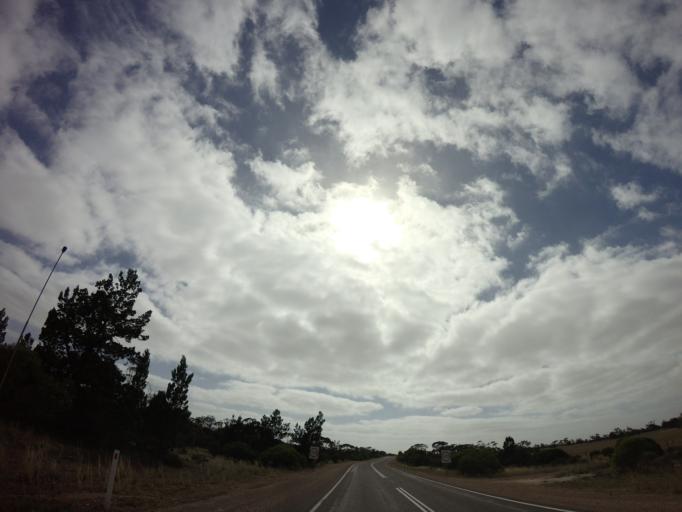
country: AU
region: South Australia
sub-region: Streaky Bay
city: Streaky Bay
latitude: -32.7233
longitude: 134.8430
